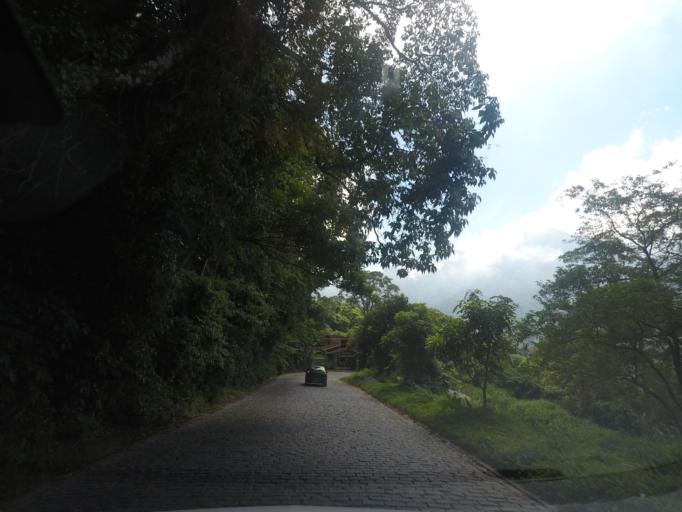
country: BR
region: Rio de Janeiro
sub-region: Petropolis
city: Petropolis
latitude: -22.5431
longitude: -43.1815
